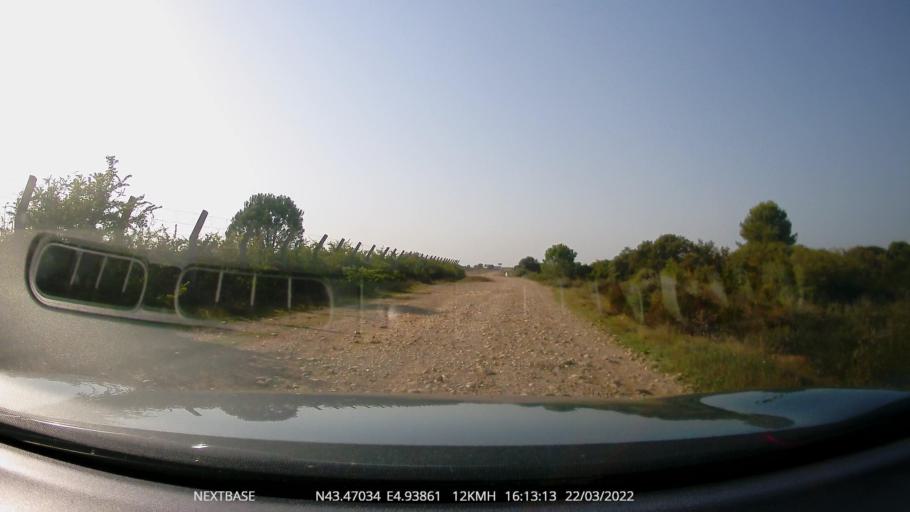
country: FR
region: Provence-Alpes-Cote d'Azur
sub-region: Departement des Bouches-du-Rhone
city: Fos-sur-Mer
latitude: 43.4705
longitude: 4.9384
